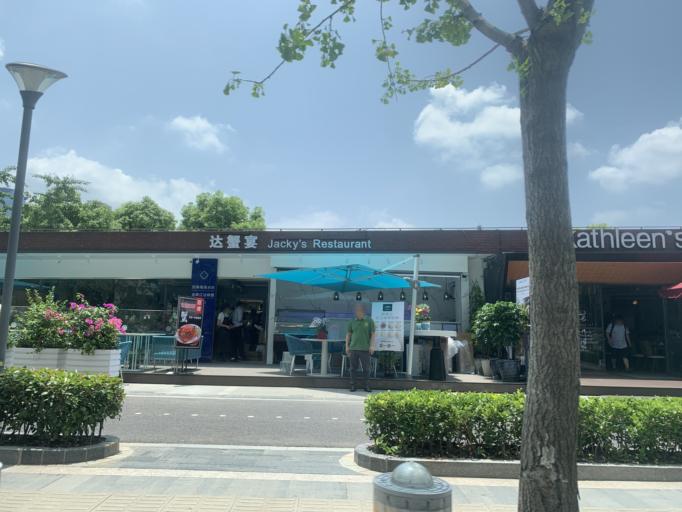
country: CN
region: Shanghai Shi
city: Hongkou
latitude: 31.2351
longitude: 121.4961
